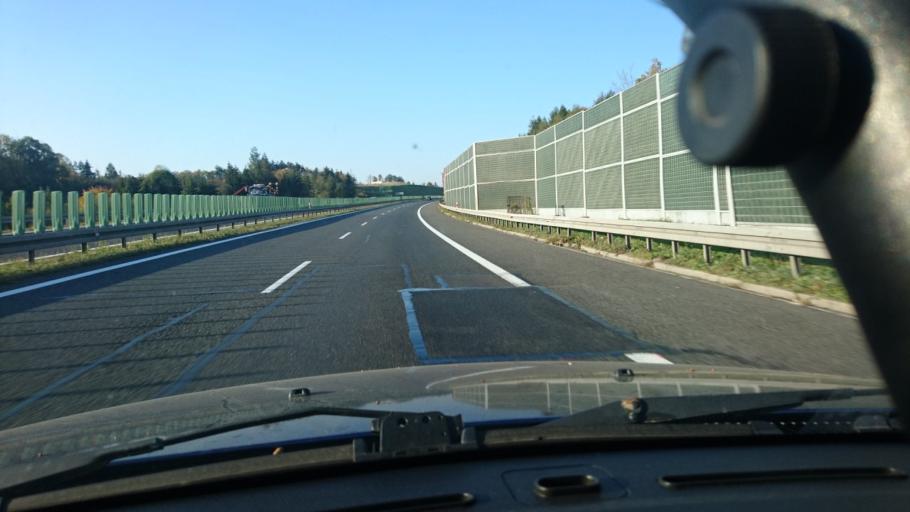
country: PL
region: Silesian Voivodeship
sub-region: Powiat cieszynski
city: Pogorze
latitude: 49.8022
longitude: 18.8482
